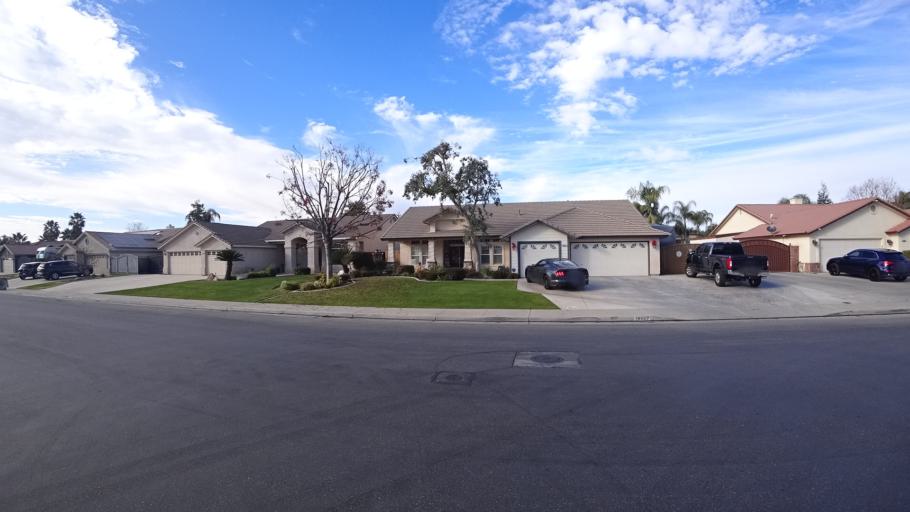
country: US
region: California
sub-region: Kern County
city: Greenacres
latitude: 35.4026
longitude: -119.1136
